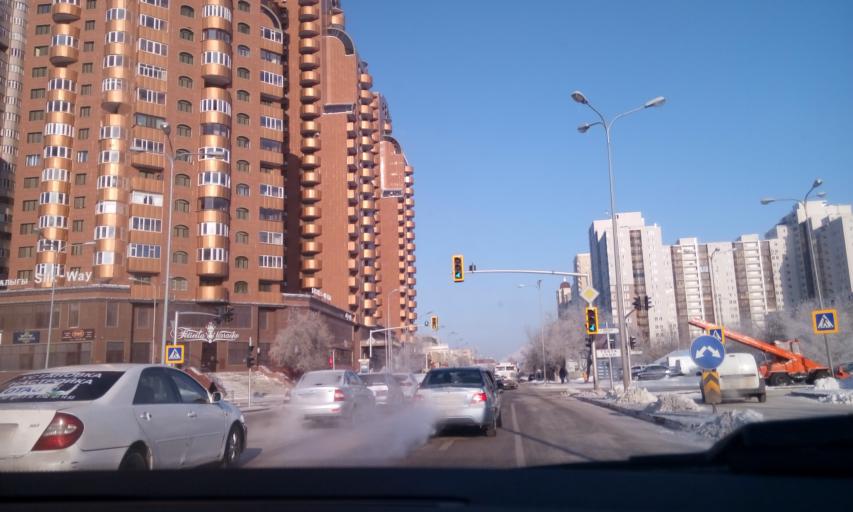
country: KZ
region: Astana Qalasy
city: Astana
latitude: 51.1638
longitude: 71.4411
